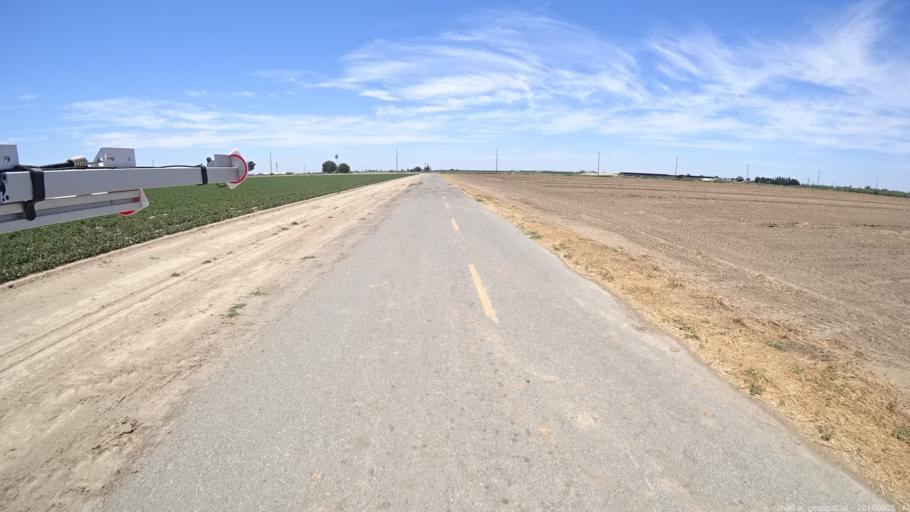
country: US
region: California
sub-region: Madera County
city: Chowchilla
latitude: 37.1055
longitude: -120.3075
